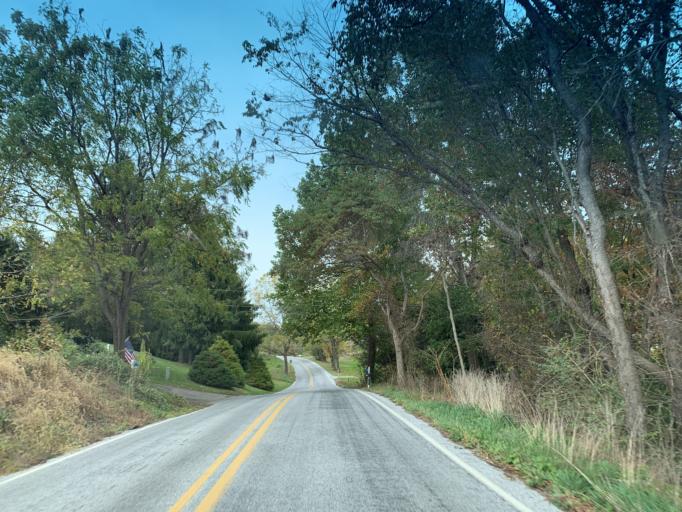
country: US
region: Pennsylvania
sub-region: York County
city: Windsor
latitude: 39.8479
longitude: -76.5107
